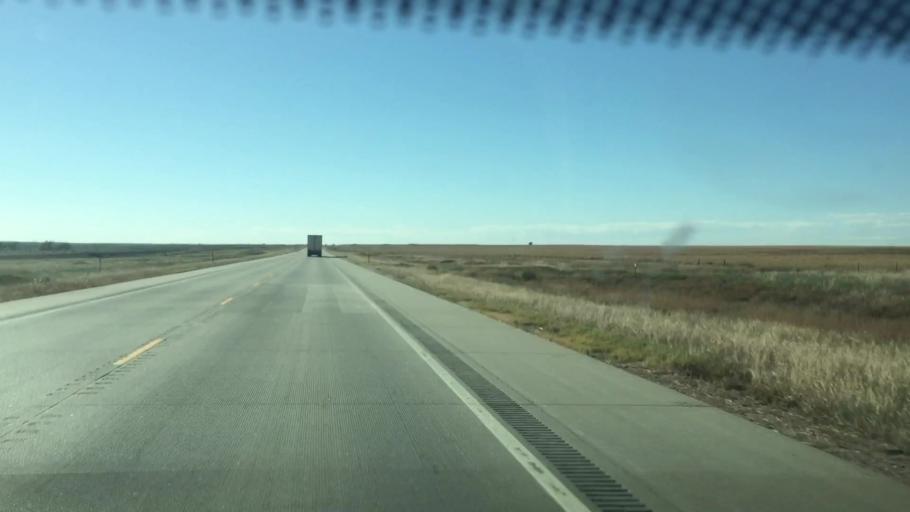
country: US
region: Colorado
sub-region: Kiowa County
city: Eads
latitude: 38.7645
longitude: -102.8309
